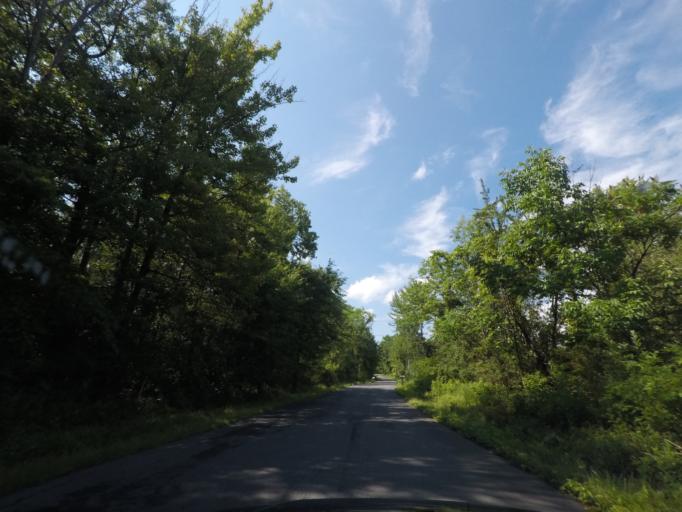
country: US
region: New York
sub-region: Rensselaer County
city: Averill Park
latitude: 42.5982
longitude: -73.5808
